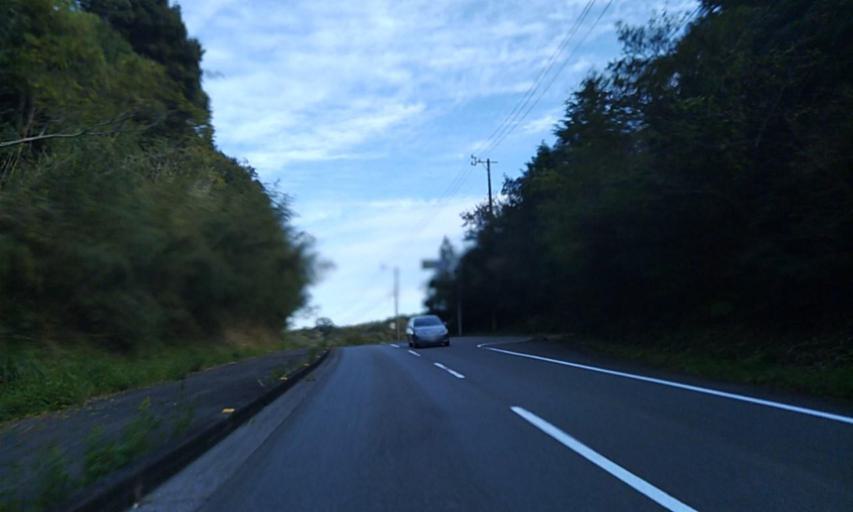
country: JP
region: Mie
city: Ise
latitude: 34.3557
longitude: 136.7503
